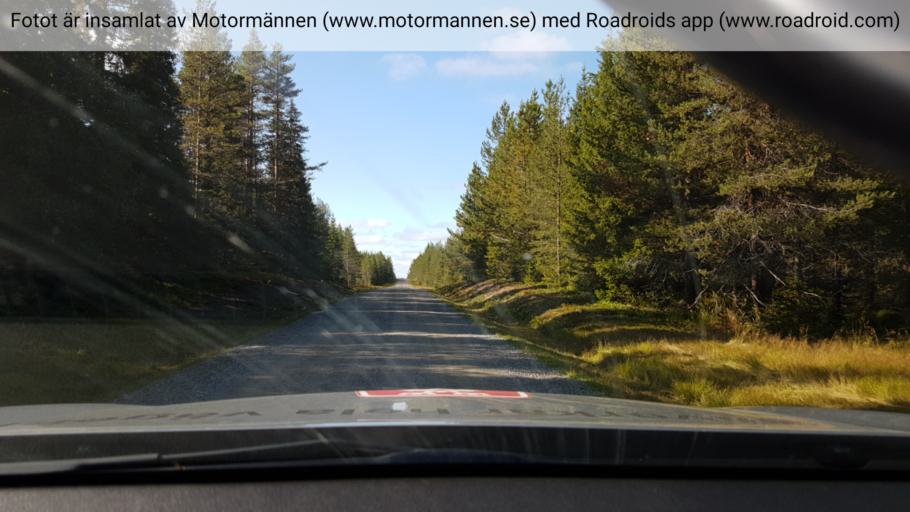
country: SE
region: Vaesterbotten
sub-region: Mala Kommun
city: Mala
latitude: 65.2123
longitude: 19.0943
